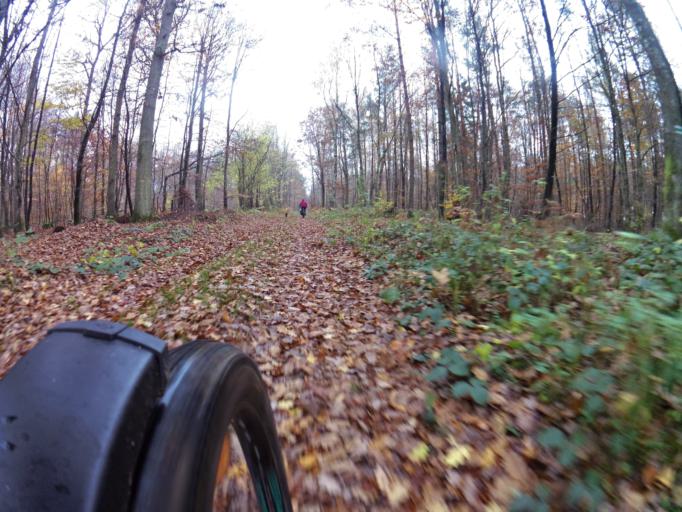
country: PL
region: Pomeranian Voivodeship
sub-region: Powiat pucki
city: Krokowa
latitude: 54.7340
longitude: 18.1310
